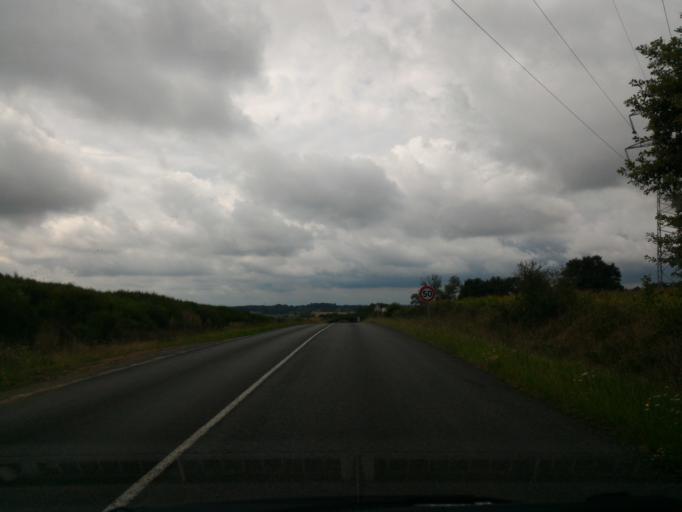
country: FR
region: Poitou-Charentes
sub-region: Departement de la Charente
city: Etagnac
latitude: 45.8823
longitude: 0.7562
